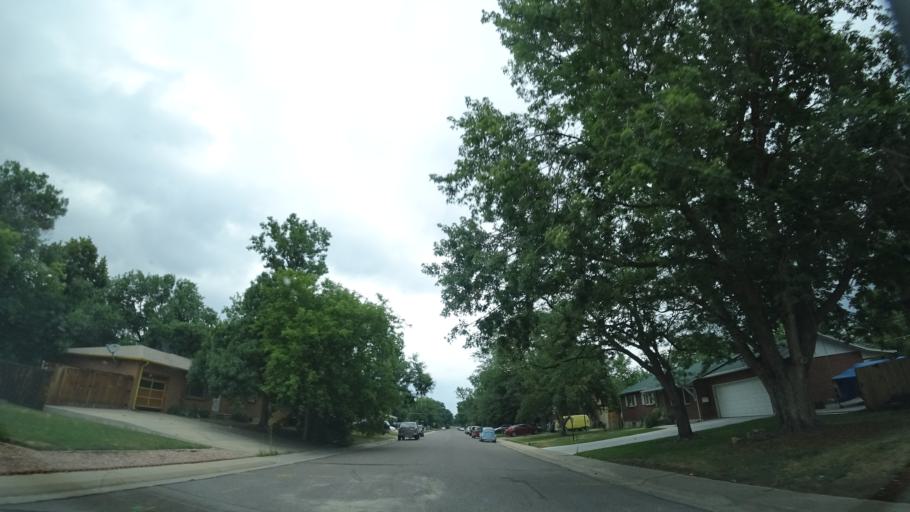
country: US
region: Colorado
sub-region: Jefferson County
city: Lakewood
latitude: 39.7061
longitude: -105.1304
